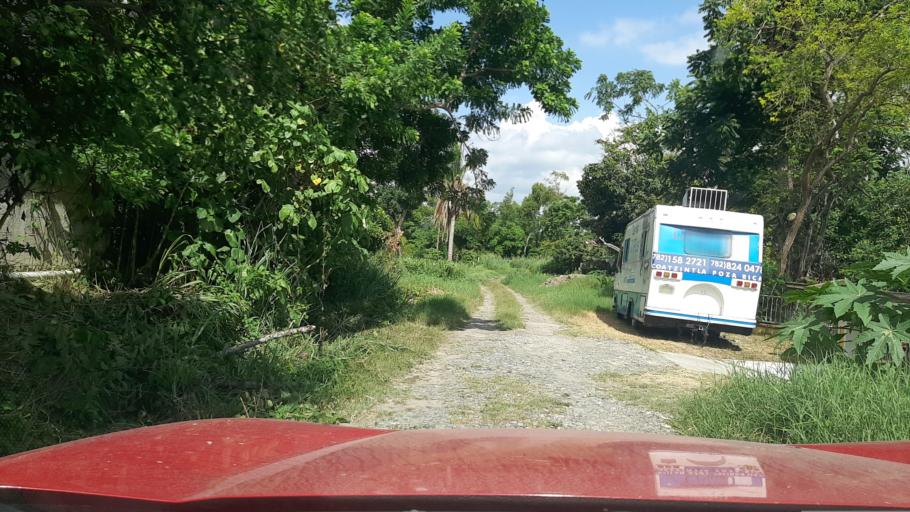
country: MX
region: Veracruz
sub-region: Poza Rica de Hidalgo
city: Villa de las Flores
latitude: 20.5744
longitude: -97.4352
